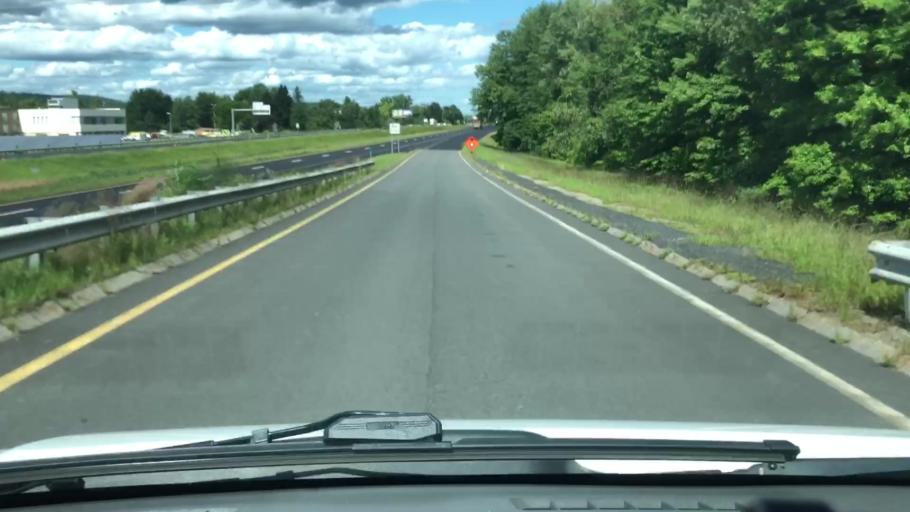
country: US
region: Massachusetts
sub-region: Hampshire County
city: Northampton
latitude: 42.3622
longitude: -72.6356
